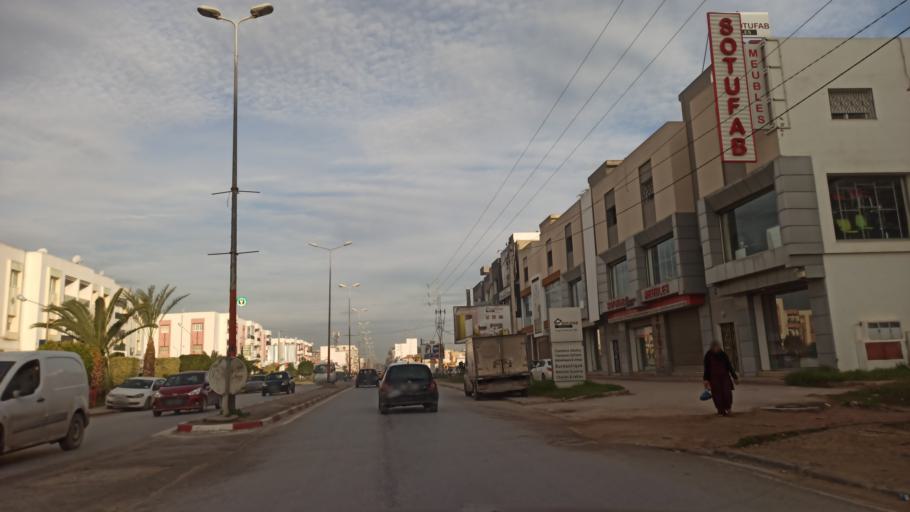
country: TN
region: Ariana
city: Ariana
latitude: 36.8632
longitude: 10.2535
